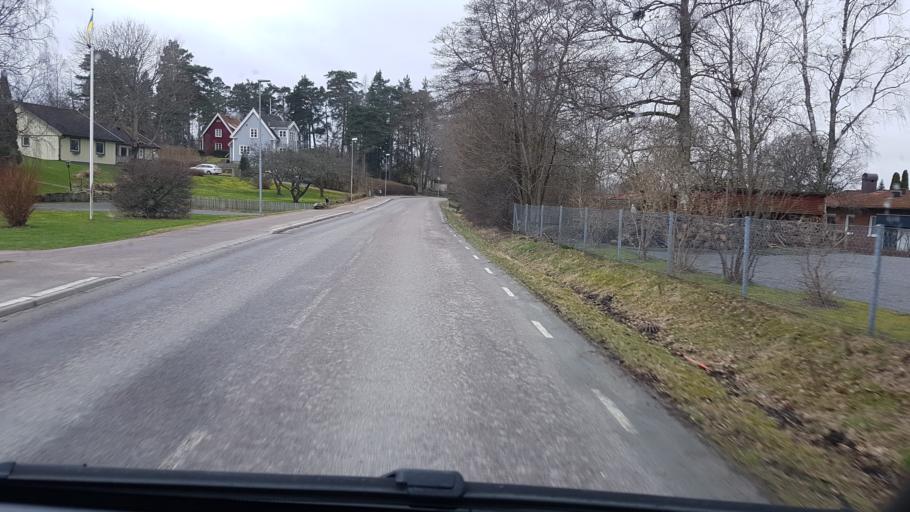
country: SE
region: Vaestra Goetaland
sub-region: Lerums Kommun
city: Stenkullen
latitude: 57.8014
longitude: 12.3760
